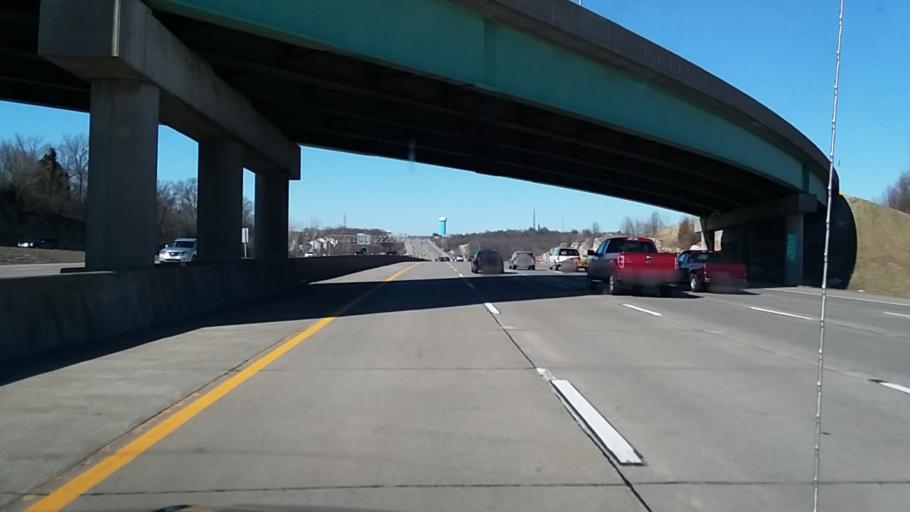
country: US
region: Missouri
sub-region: Jefferson County
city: Arnold
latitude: 38.4175
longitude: -90.3882
